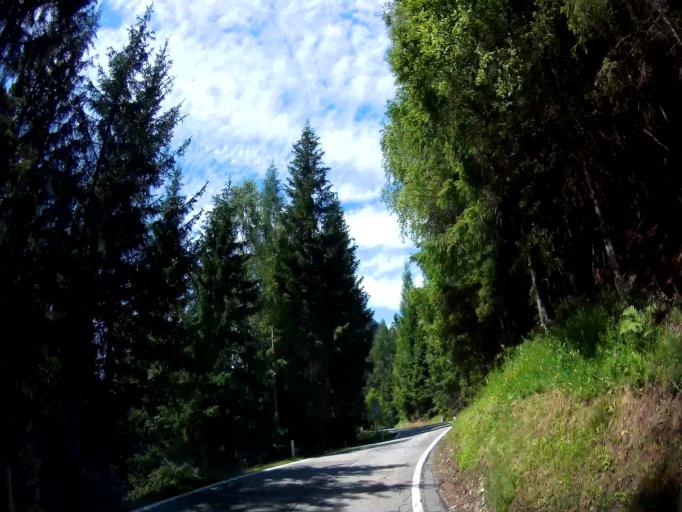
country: AT
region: Carinthia
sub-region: Politischer Bezirk Sankt Veit an der Glan
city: Glodnitz
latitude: 46.9324
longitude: 14.0537
